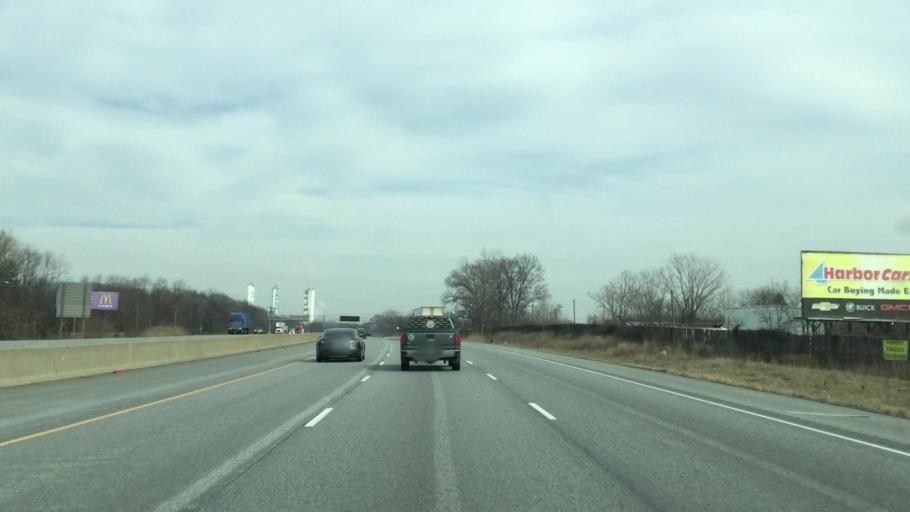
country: US
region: Indiana
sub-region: Porter County
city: Burns Harbor
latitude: 41.6024
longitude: -87.1431
